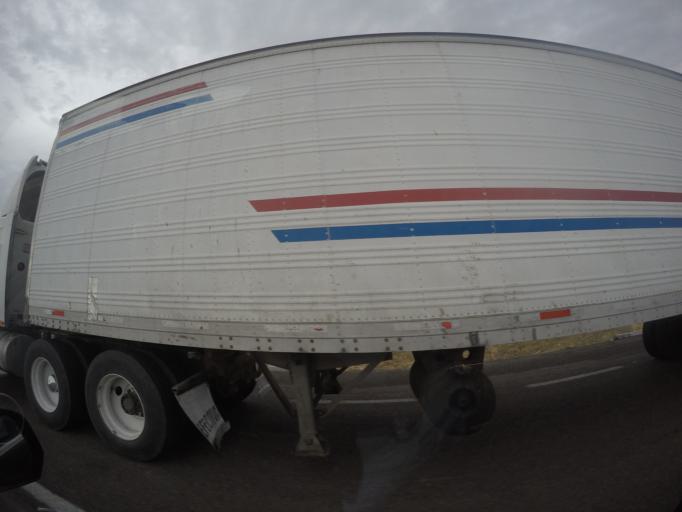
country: MX
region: Guanajuato
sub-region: Irapuato
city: Serrano
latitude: 20.8088
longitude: -101.4355
